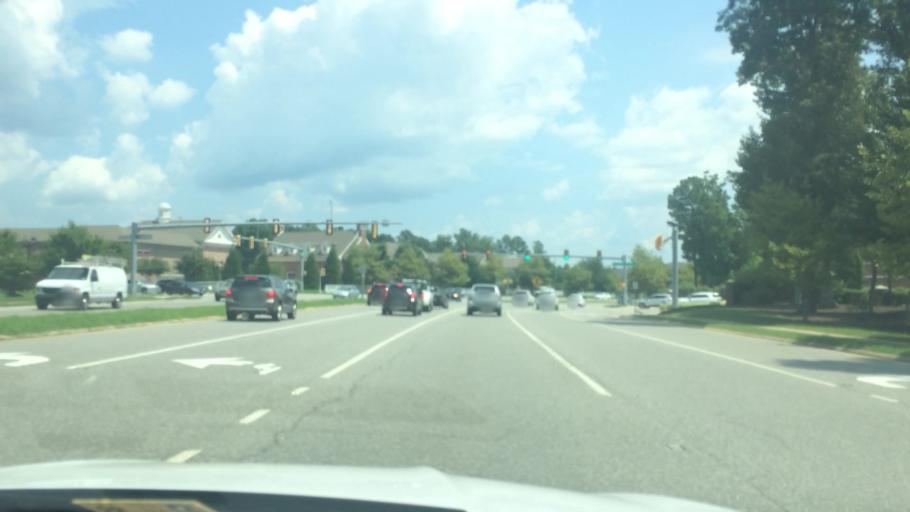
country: US
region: Virginia
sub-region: James City County
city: Williamsburg
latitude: 37.2758
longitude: -76.7484
